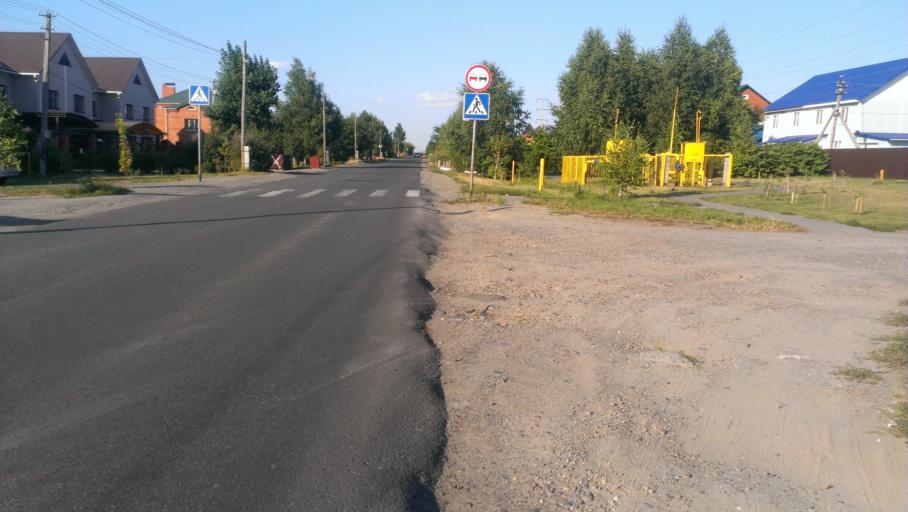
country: RU
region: Altai Krai
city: Novosilikatnyy
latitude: 53.3596
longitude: 83.6401
